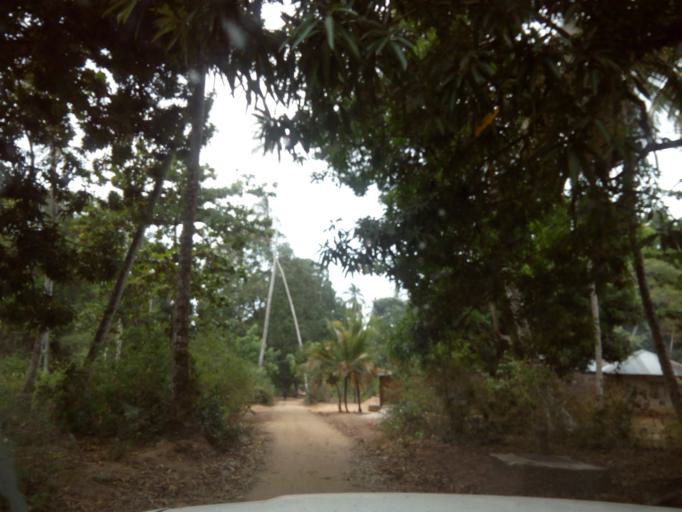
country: TZ
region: Zanzibar Central/South
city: Mahonda
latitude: -6.3304
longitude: 39.3972
